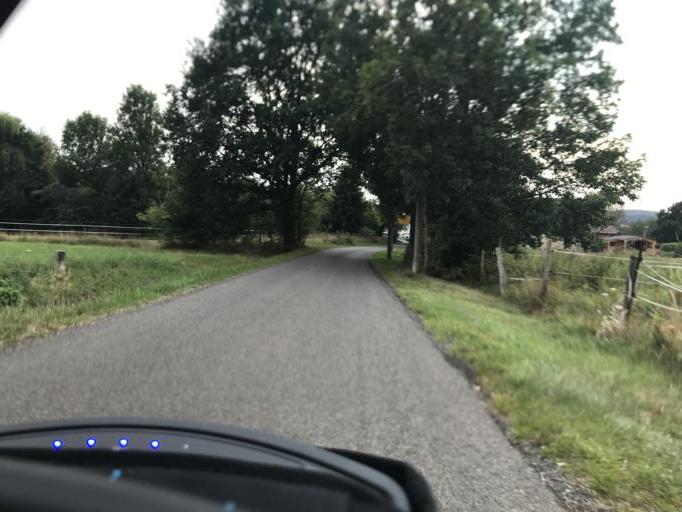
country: DE
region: North Rhine-Westphalia
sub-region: Regierungsbezirk Koln
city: Stossdorf
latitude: 50.7527
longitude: 7.2423
